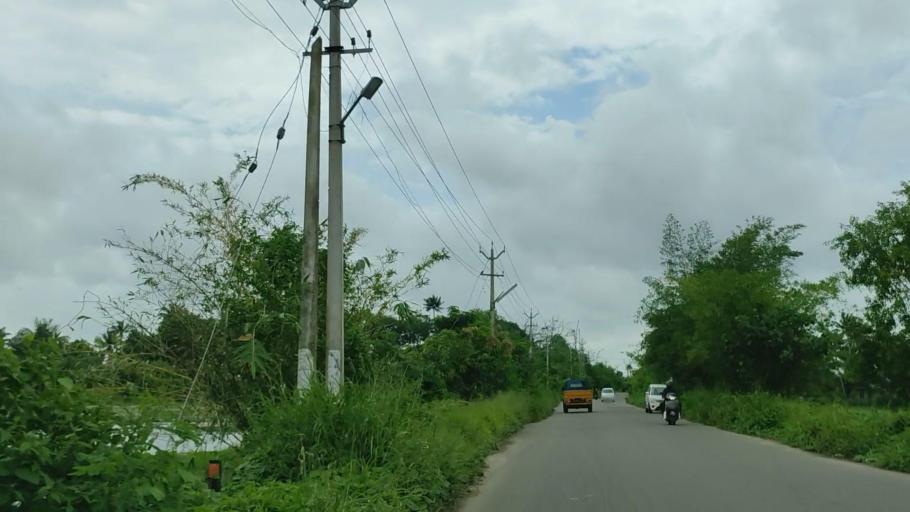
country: IN
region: Kerala
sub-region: Kottayam
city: Kottayam
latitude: 9.5656
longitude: 76.5070
